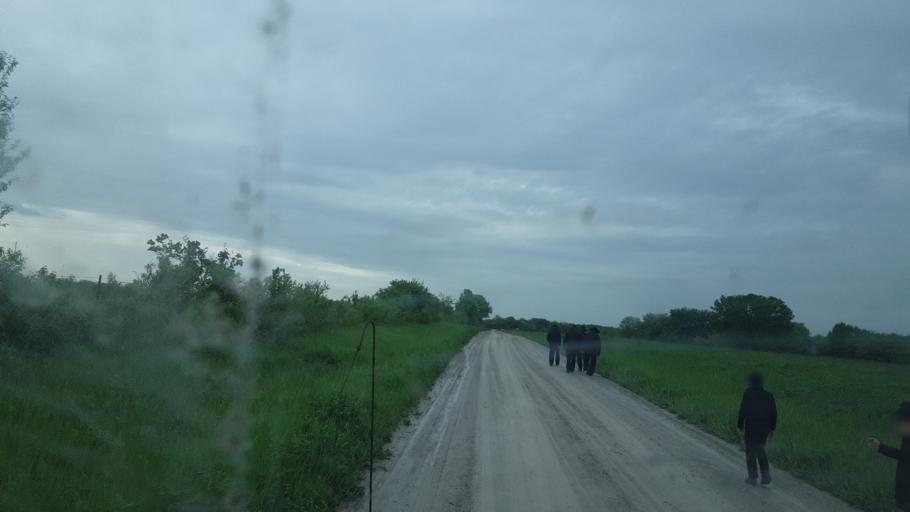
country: US
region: Missouri
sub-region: Clark County
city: Kahoka
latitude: 40.4358
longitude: -91.6157
